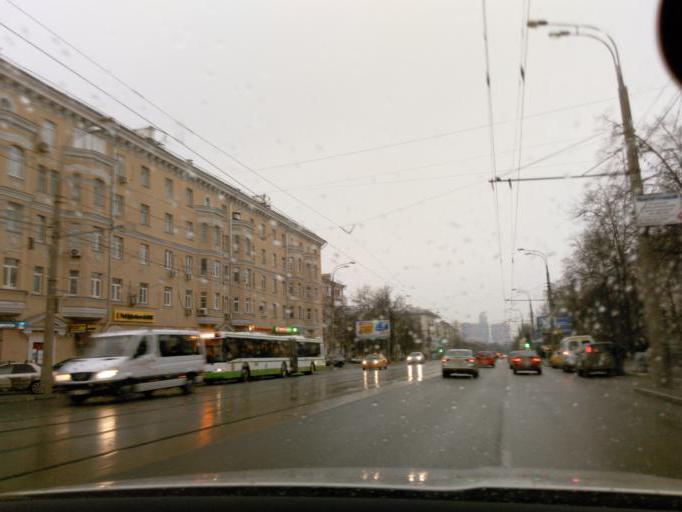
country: RU
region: Moscow
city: Pokrovskoye-Streshnevo
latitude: 55.8339
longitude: 37.4537
